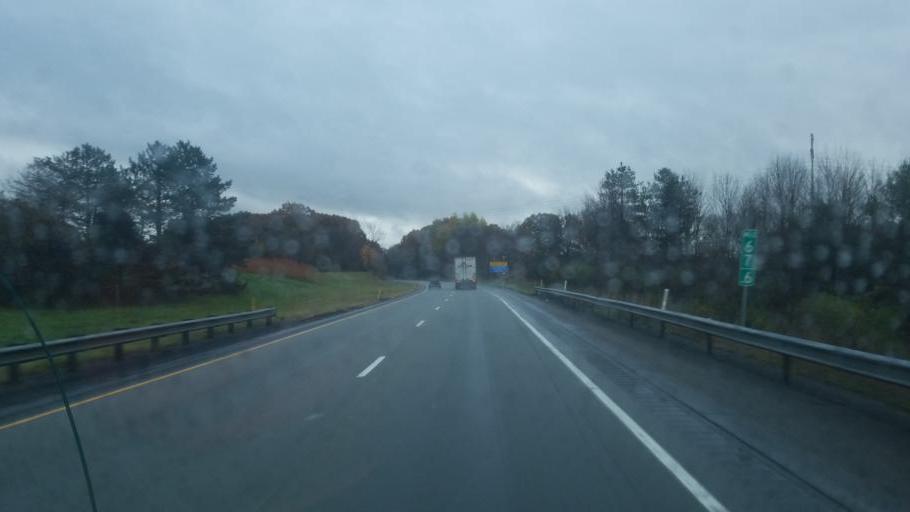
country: US
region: Pennsylvania
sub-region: Clarion County
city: Clarion
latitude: 41.1755
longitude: -79.2949
